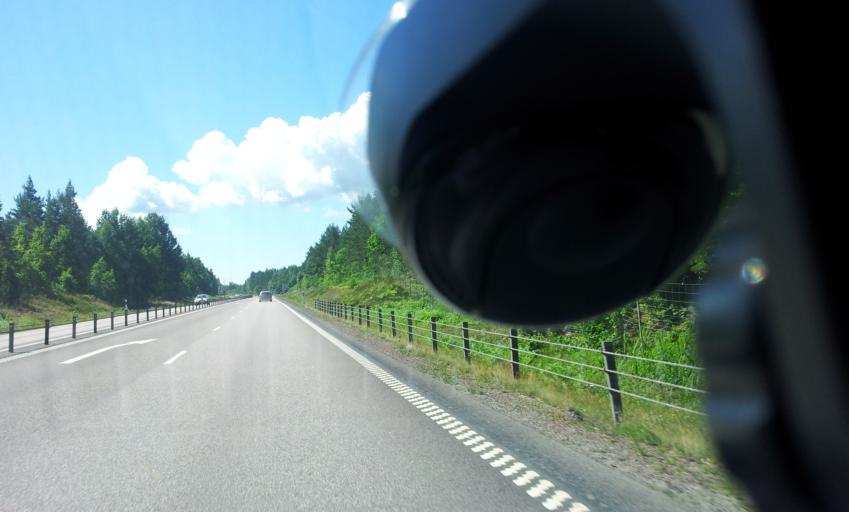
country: SE
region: Kalmar
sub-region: Oskarshamns Kommun
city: Paskallavik
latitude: 57.2013
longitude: 16.4378
